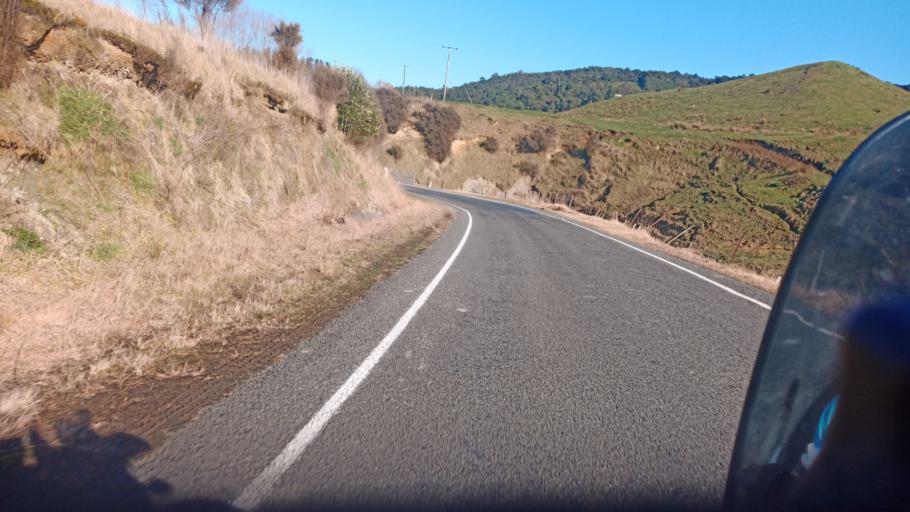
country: NZ
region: Gisborne
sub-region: Gisborne District
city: Gisborne
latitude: -38.5835
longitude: 177.5413
